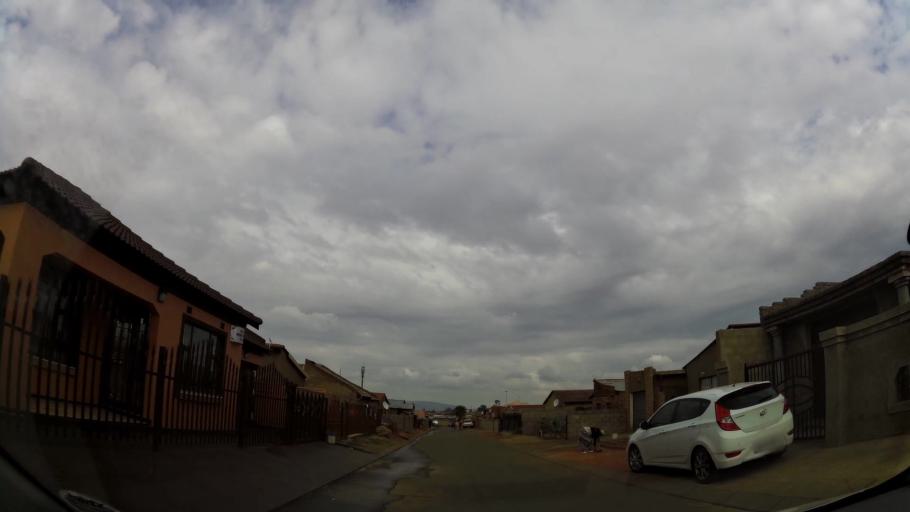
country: ZA
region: Gauteng
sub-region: Ekurhuleni Metropolitan Municipality
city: Germiston
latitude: -26.3781
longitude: 28.1617
